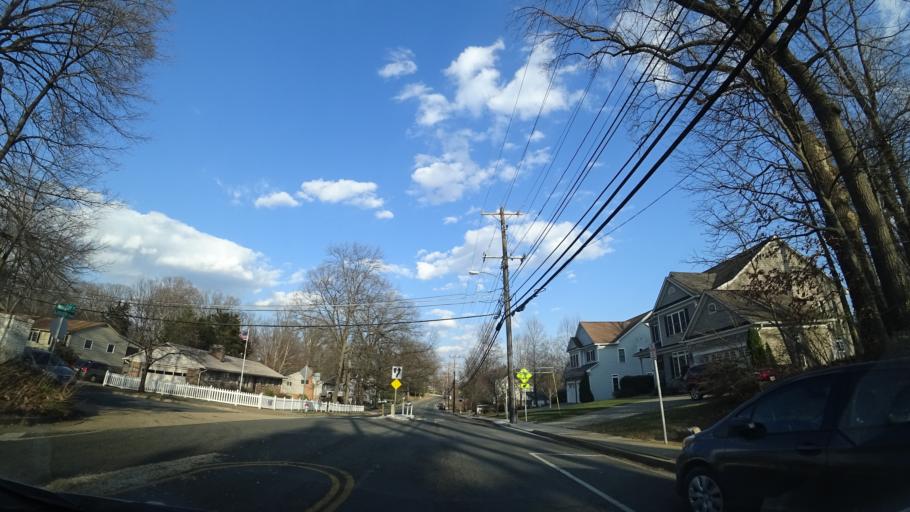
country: US
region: Virginia
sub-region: City of Falls Church
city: Falls Church
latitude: 38.8903
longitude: -77.1720
